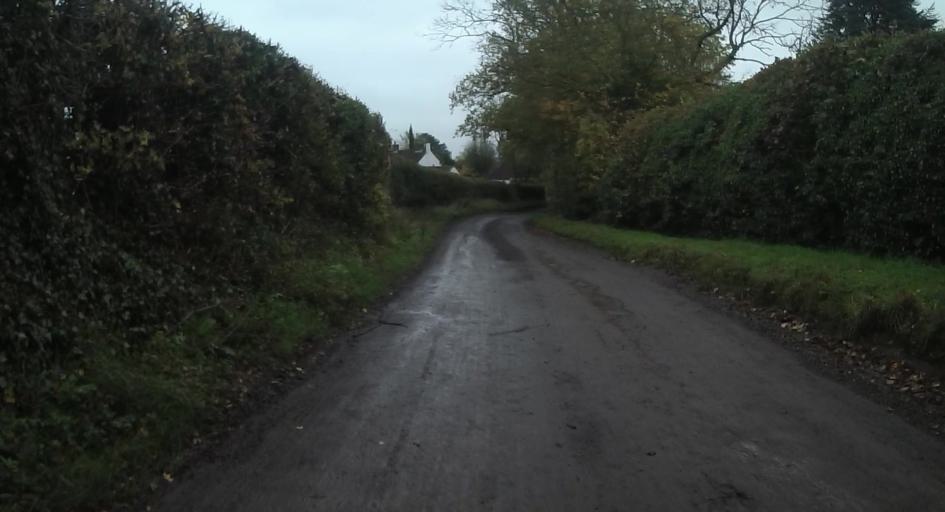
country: GB
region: England
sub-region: Surrey
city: Farnham
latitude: 51.2209
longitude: -0.8078
